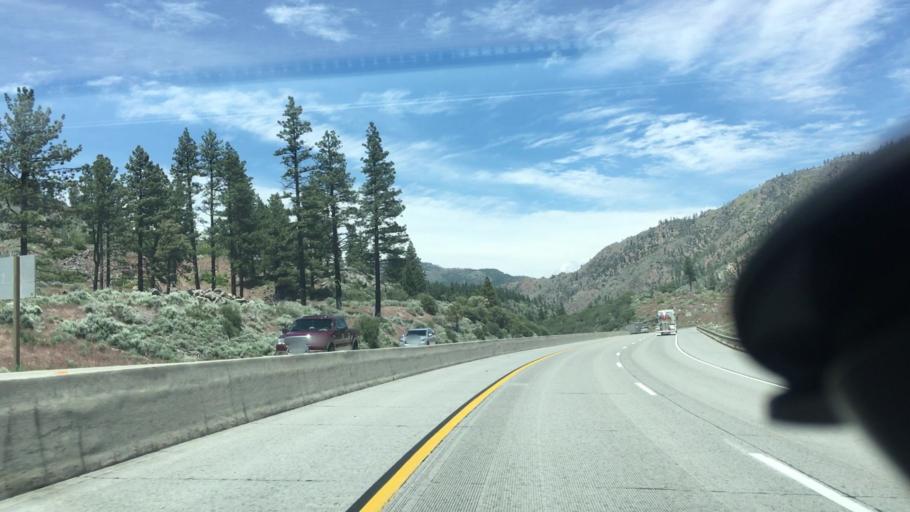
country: US
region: Nevada
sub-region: Washoe County
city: Verdi
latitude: 39.3866
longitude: -120.0250
